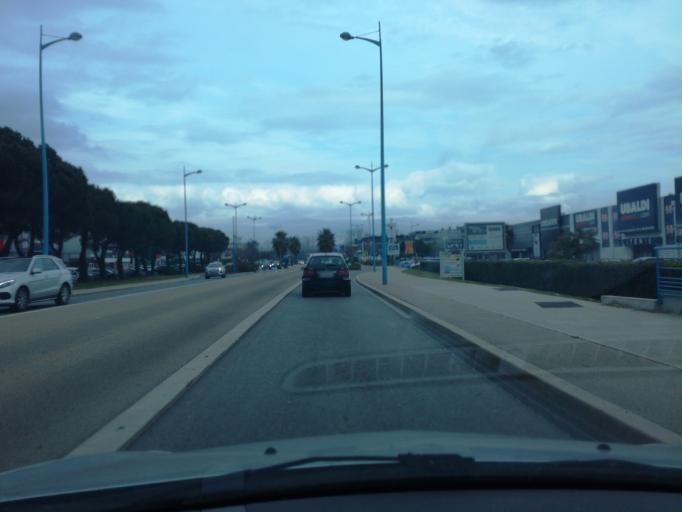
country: FR
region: Provence-Alpes-Cote d'Azur
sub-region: Departement des Alpes-Maritimes
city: Mandelieu-la-Napoule
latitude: 43.5534
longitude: 6.9549
